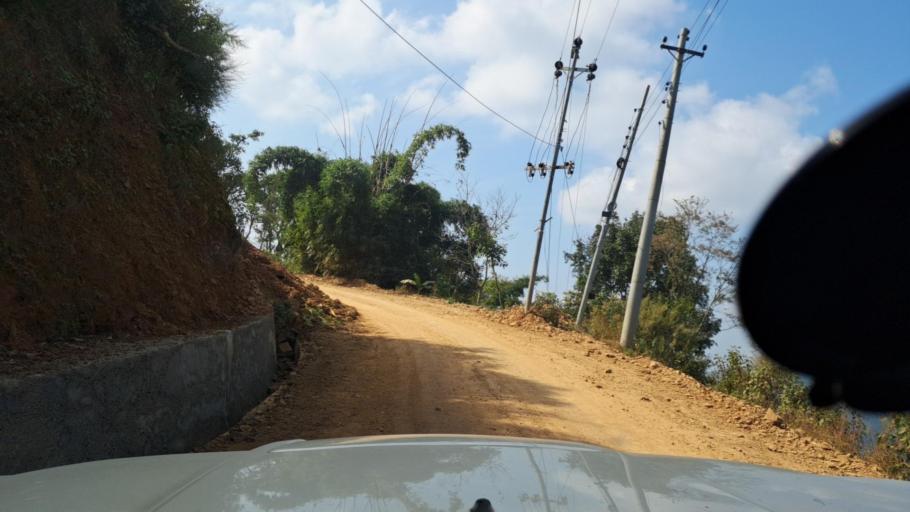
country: NP
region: Western Region
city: Tansen
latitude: 27.8213
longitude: 83.6852
